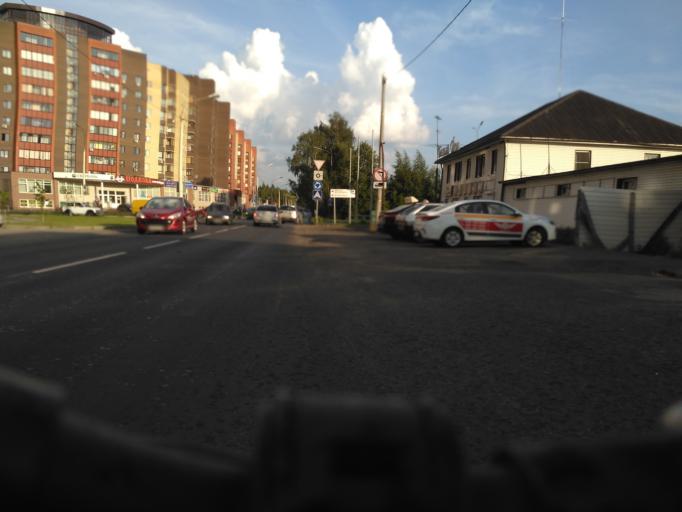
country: RU
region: Moskovskaya
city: Dubna
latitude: 56.7291
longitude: 37.1398
